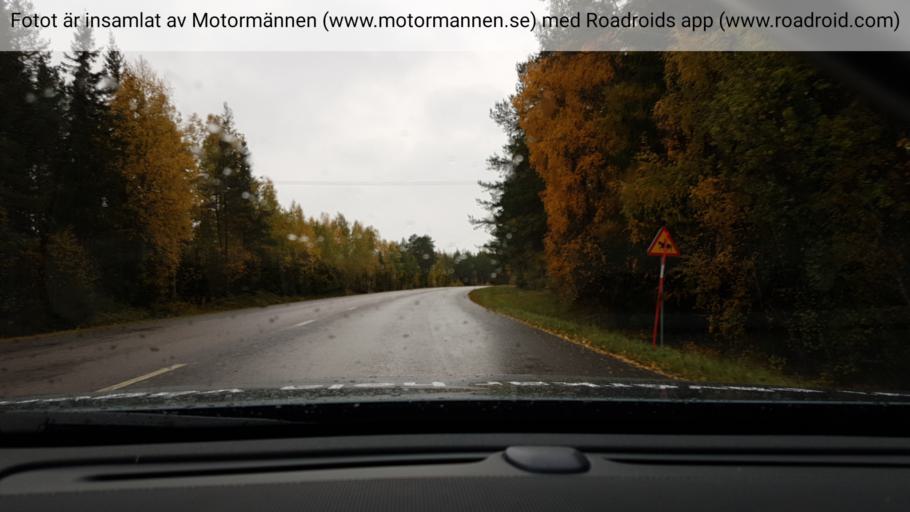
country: SE
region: Norrbotten
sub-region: Lulea Kommun
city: Gammelstad
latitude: 65.5834
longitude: 22.0201
